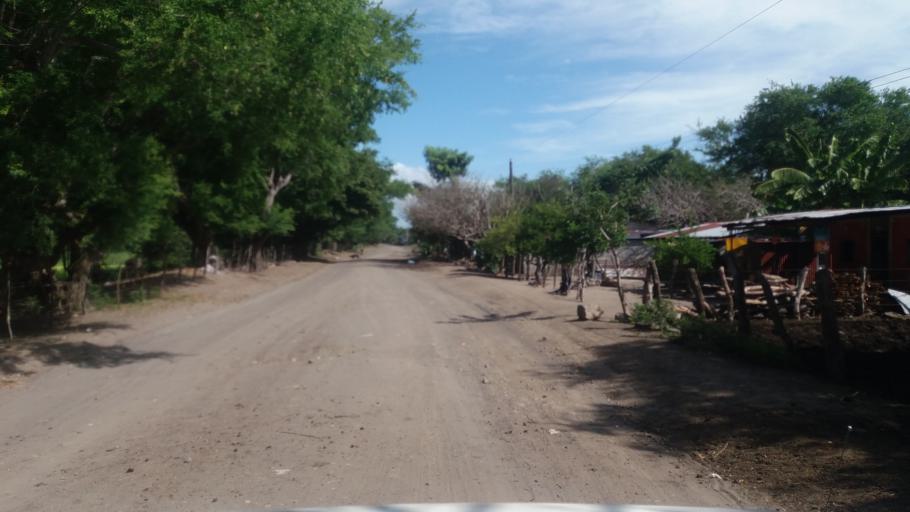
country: NI
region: Granada
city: Granada
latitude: 12.0063
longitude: -85.9335
